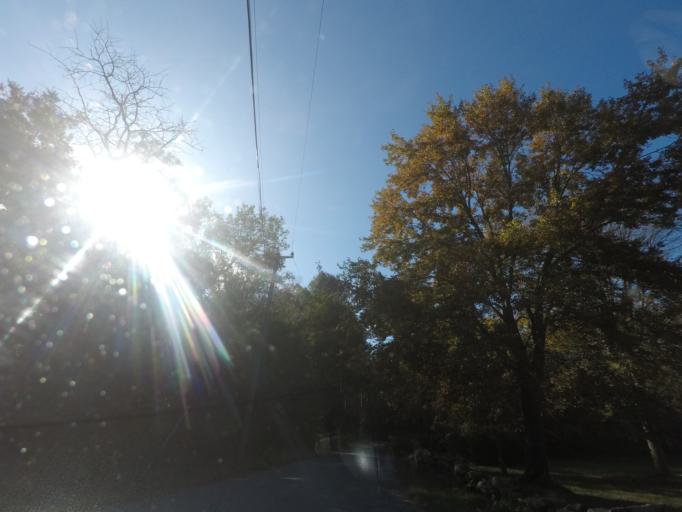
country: US
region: Connecticut
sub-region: Windham County
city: Thompson
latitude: 41.9767
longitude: -71.8293
